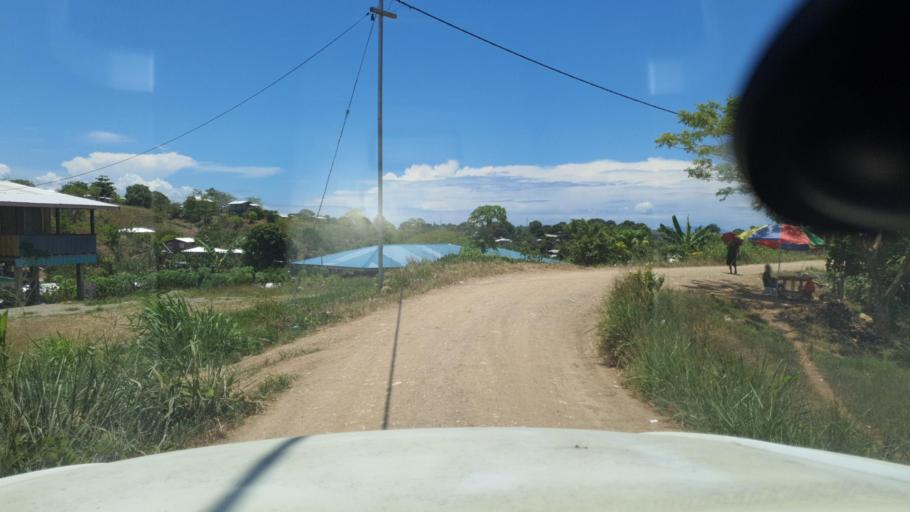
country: SB
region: Guadalcanal
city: Honiara
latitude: -9.4573
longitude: 159.9934
